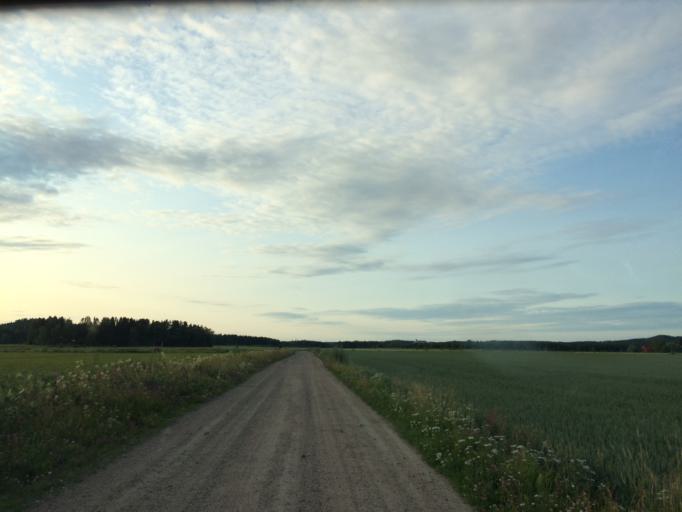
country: FI
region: Haeme
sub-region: Haemeenlinna
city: Janakkala
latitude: 60.8801
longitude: 24.6300
